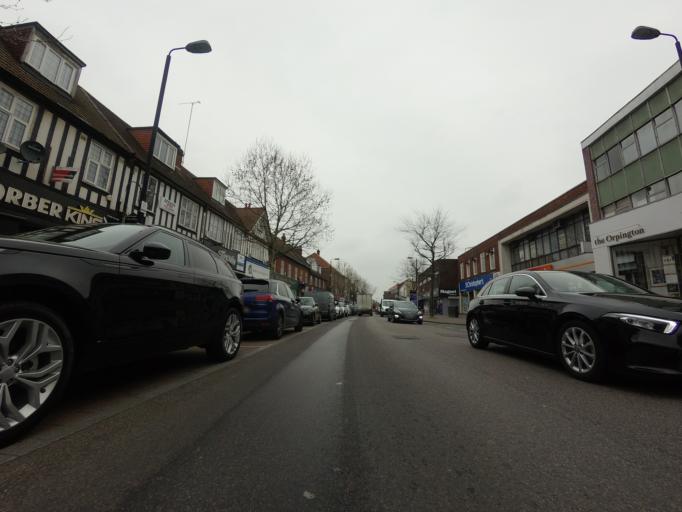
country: GB
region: England
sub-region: Greater London
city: Orpington
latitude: 51.3775
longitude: 0.1004
